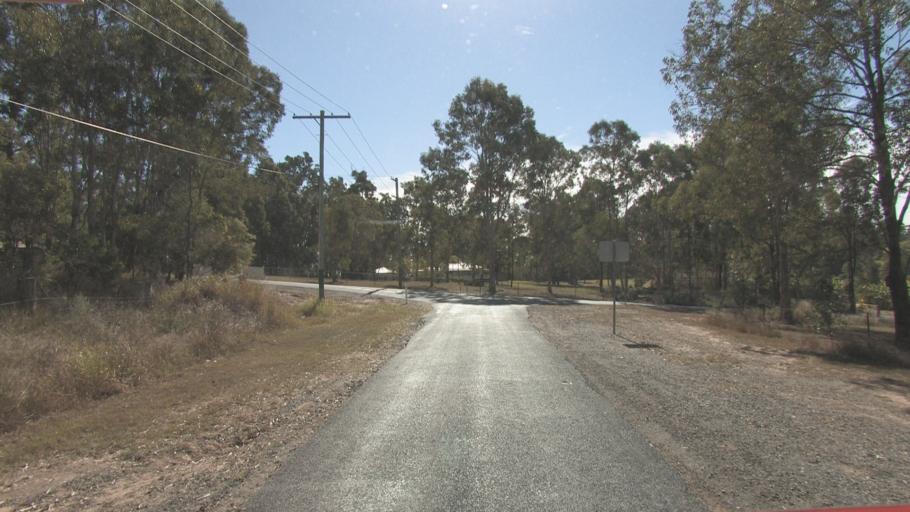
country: AU
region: Queensland
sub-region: Ipswich
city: Springfield Lakes
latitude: -27.7050
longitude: 152.9416
